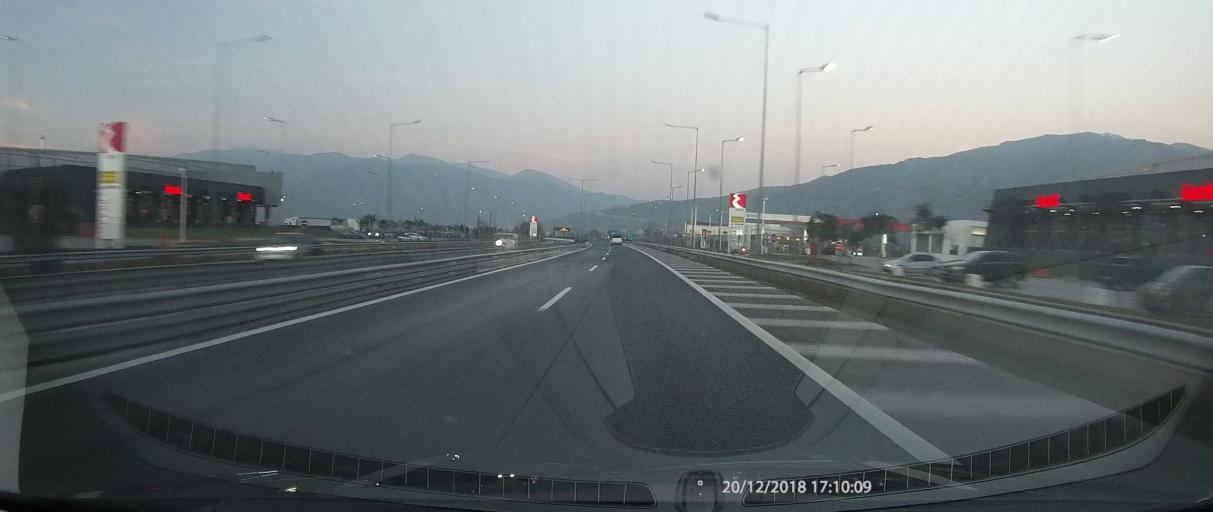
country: GR
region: Thessaly
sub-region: Nomos Larisis
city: Makrychori
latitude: 39.8139
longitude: 22.5077
